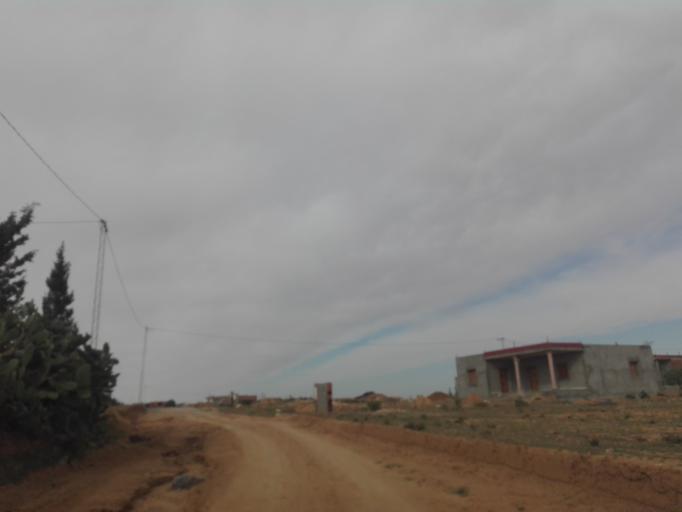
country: TN
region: Safaqis
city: Sfax
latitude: 34.7329
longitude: 10.4972
